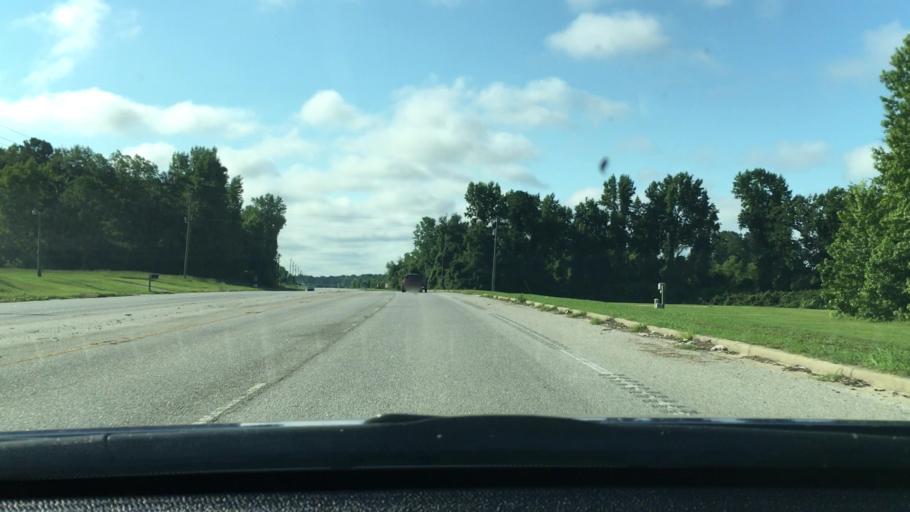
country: US
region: South Carolina
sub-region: Clarendon County
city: Manning
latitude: 33.7490
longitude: -80.2195
